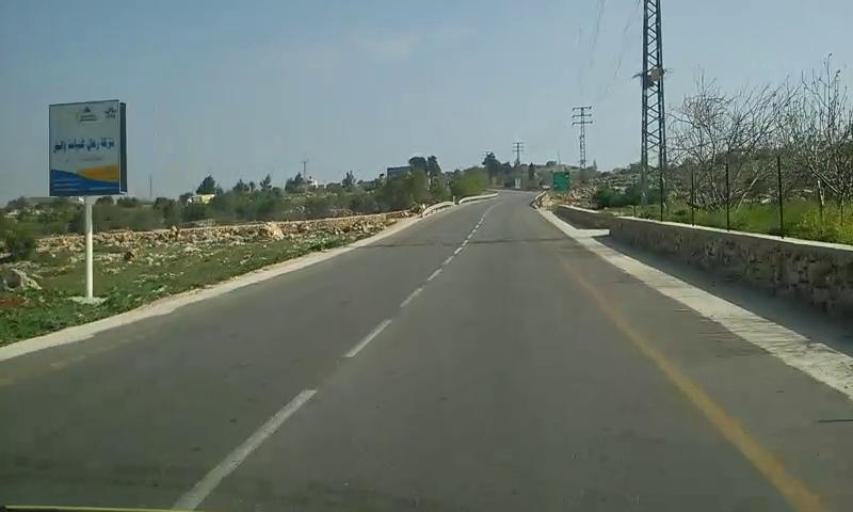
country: PS
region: West Bank
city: Silwad
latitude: 31.9679
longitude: 35.2691
